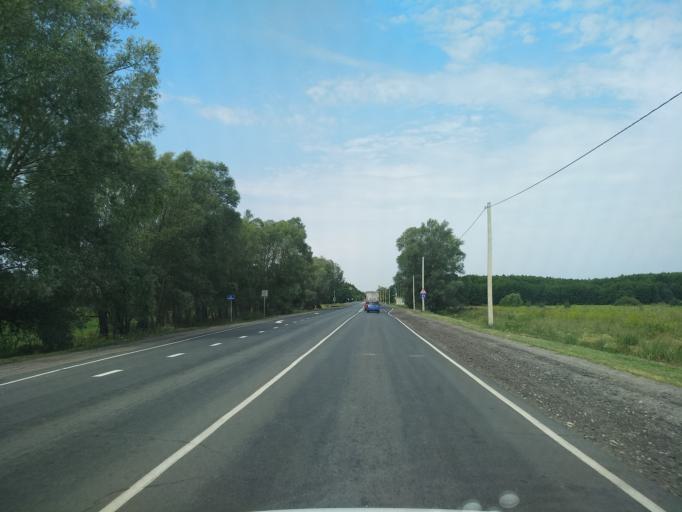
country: RU
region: Voronezj
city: Orlovo
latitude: 51.6806
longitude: 39.6026
